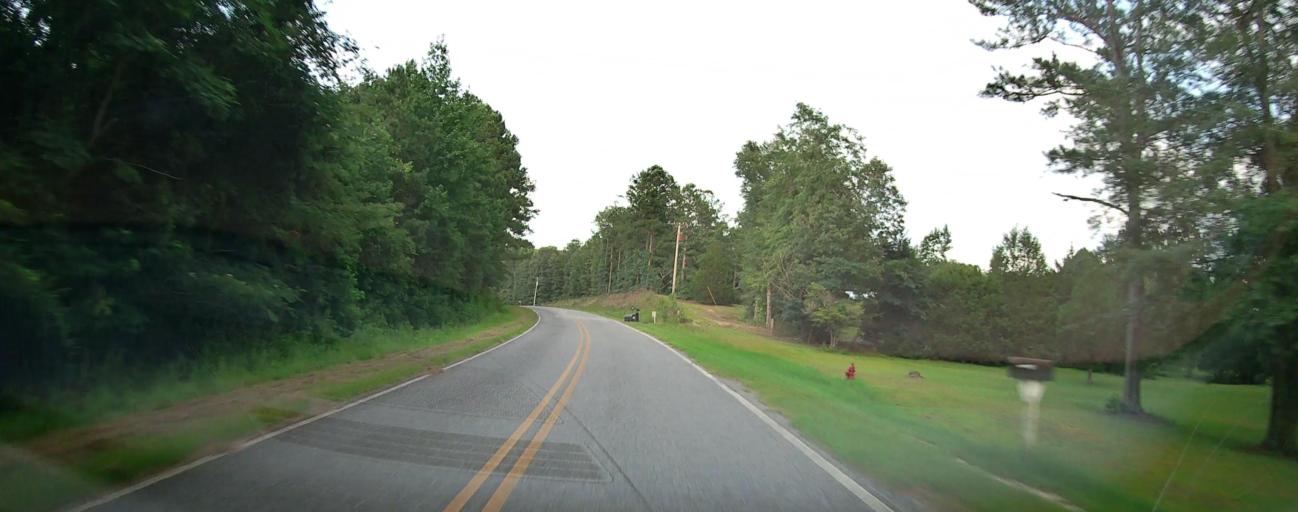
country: US
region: Georgia
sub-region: Crawford County
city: Roberta
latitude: 32.6523
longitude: -84.0298
